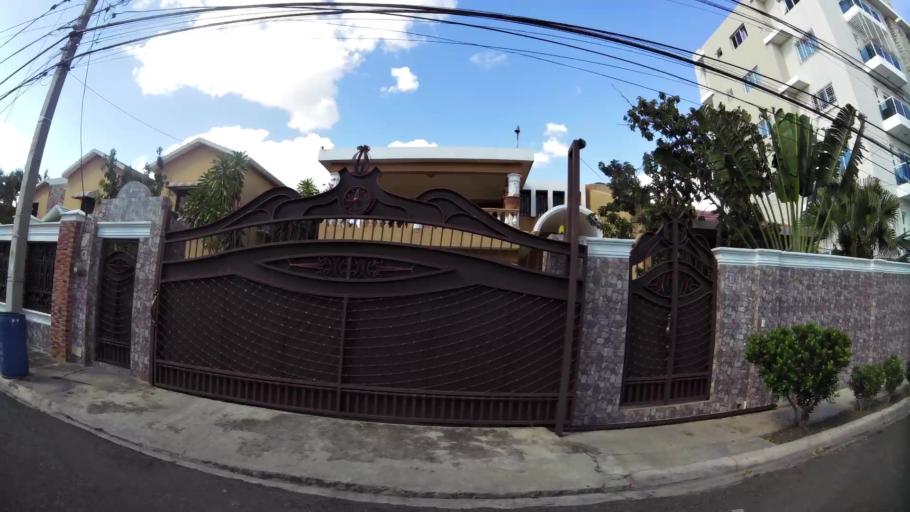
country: DO
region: Santiago
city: Santiago de los Caballeros
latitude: 19.4501
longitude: -70.6725
